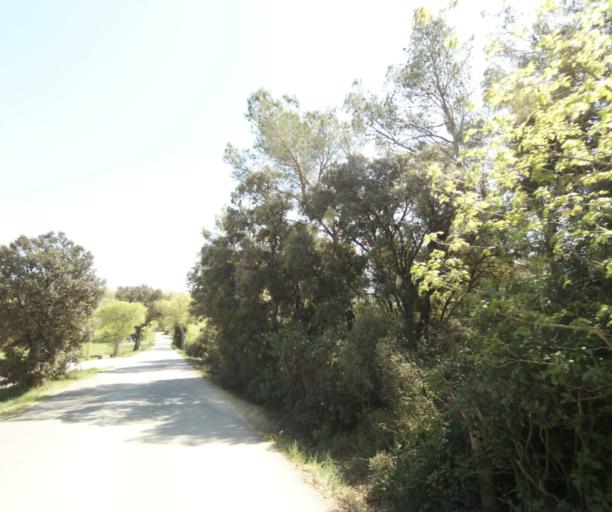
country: FR
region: Languedoc-Roussillon
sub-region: Departement de l'Herault
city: Prades-le-Lez
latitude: 43.7130
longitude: 3.8625
